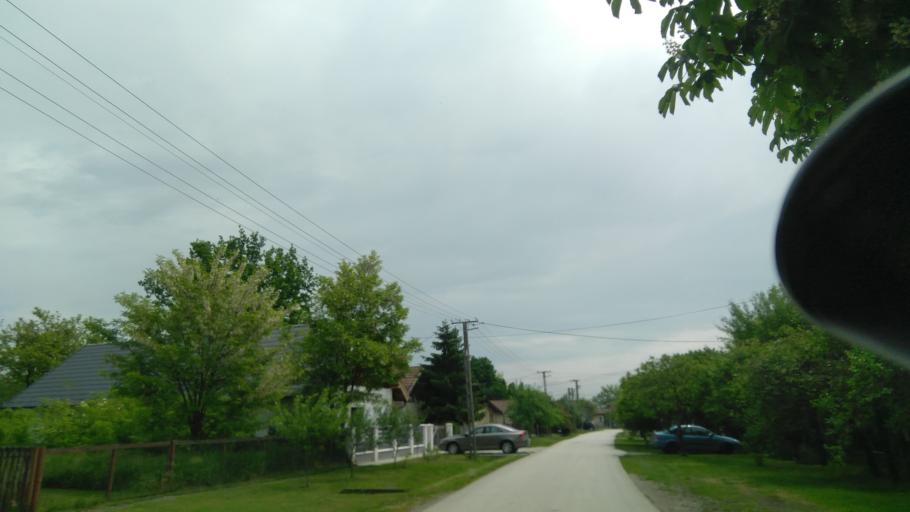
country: HU
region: Bekes
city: Fuzesgyarmat
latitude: 47.1101
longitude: 21.2215
